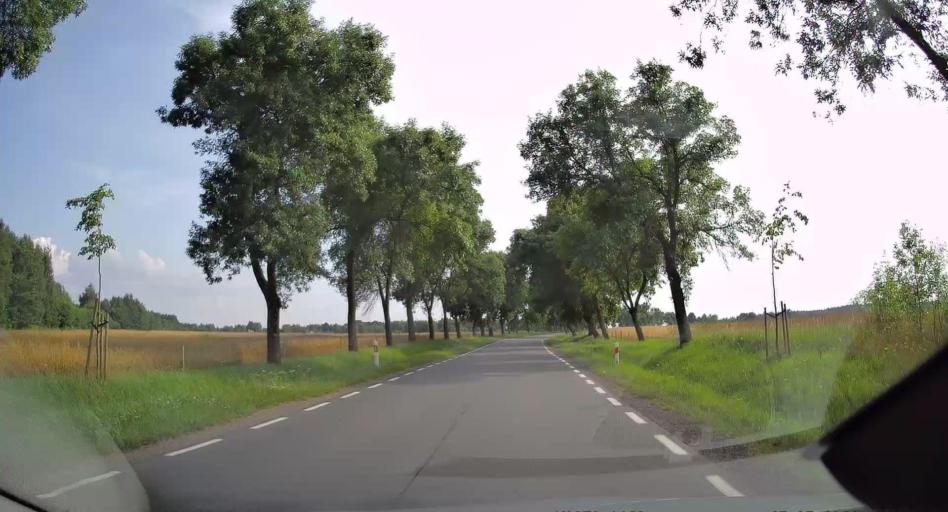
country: PL
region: Lodz Voivodeship
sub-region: Powiat tomaszowski
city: Inowlodz
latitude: 51.5362
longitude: 20.2316
